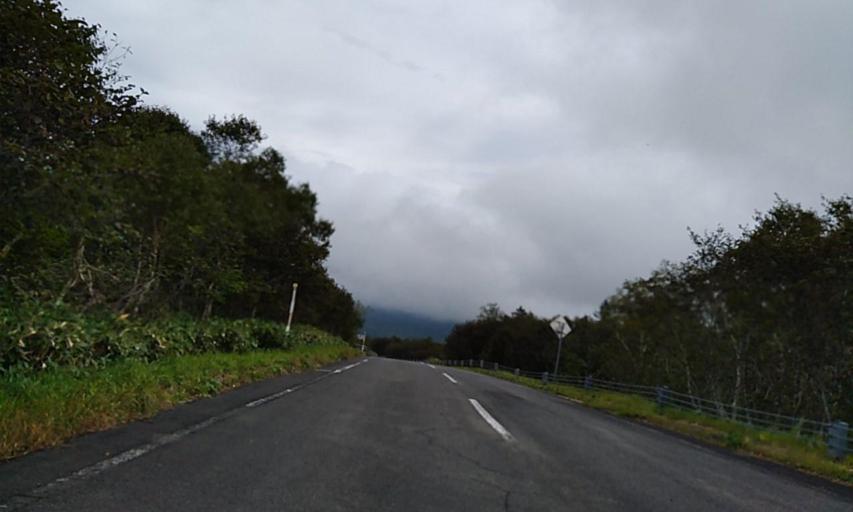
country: JP
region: Hokkaido
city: Bihoro
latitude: 43.6007
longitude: 144.5717
